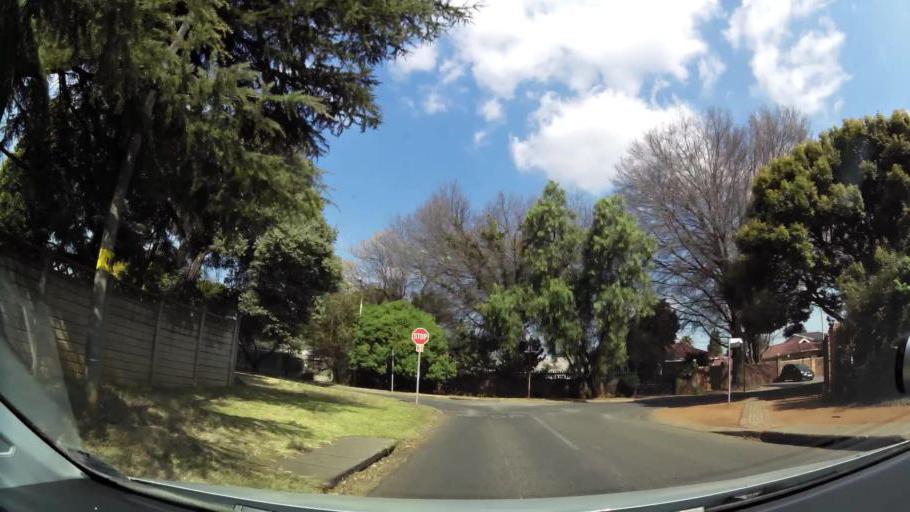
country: ZA
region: Gauteng
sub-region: City of Johannesburg Metropolitan Municipality
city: Modderfontein
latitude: -26.0835
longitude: 28.2327
